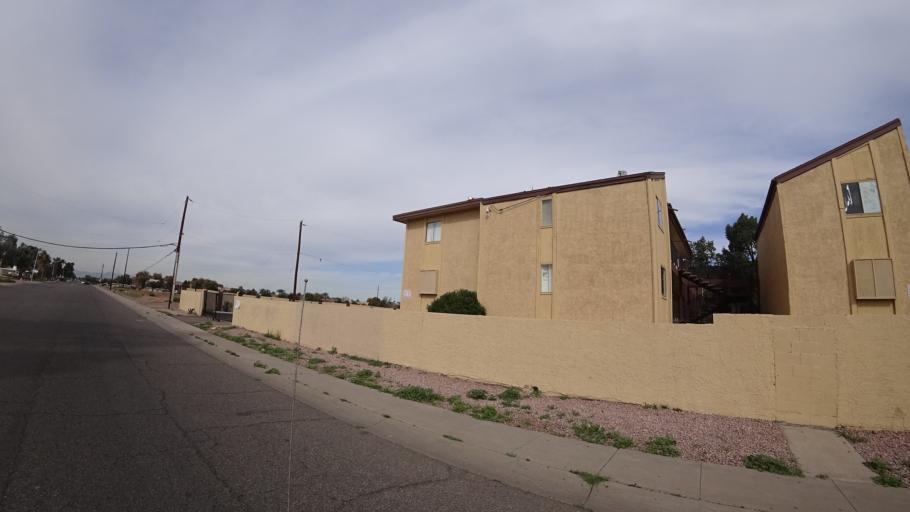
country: US
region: Arizona
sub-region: Maricopa County
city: Glendale
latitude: 33.5348
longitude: -112.2005
